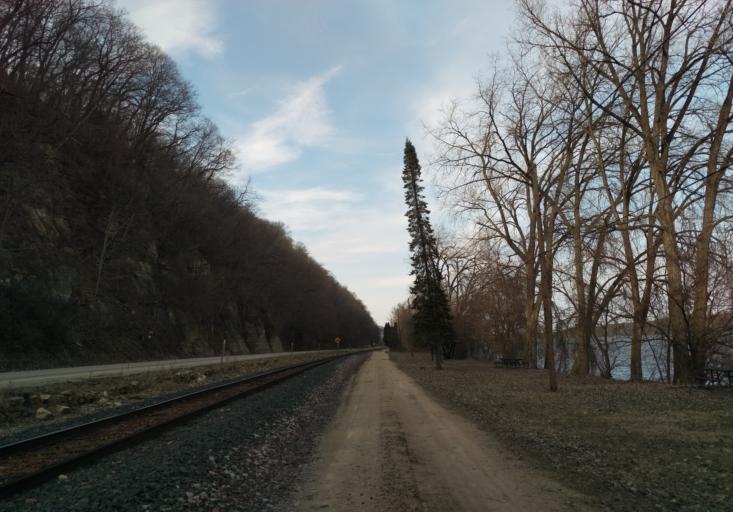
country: US
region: Wisconsin
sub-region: Crawford County
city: Prairie du Chien
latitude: 43.0688
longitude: -91.1802
